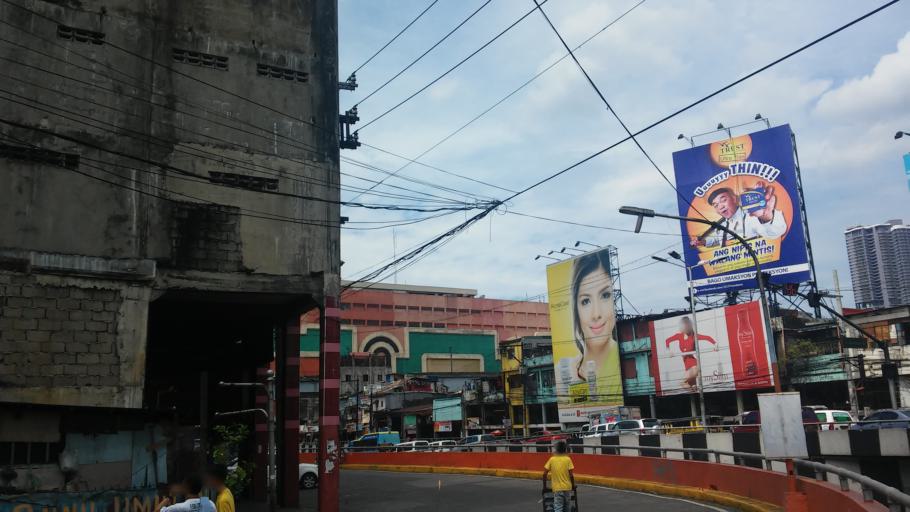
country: PH
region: Metro Manila
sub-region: City of Manila
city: Manila
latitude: 14.6046
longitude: 120.9856
